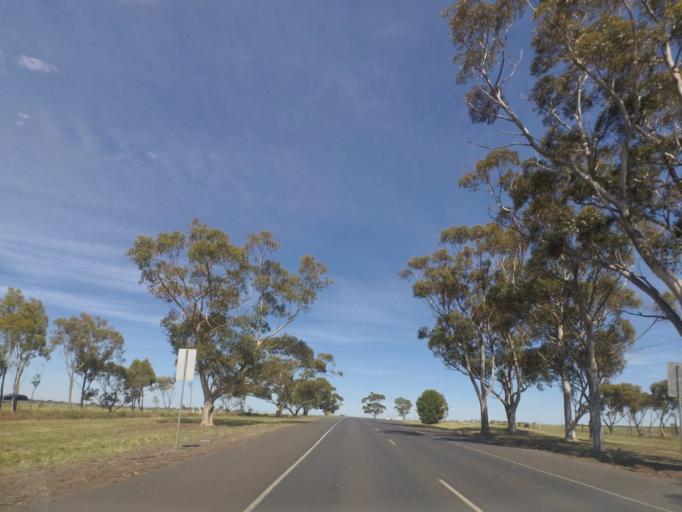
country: AU
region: Victoria
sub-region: Melton
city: Brookfield
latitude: -37.6864
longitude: 144.5364
